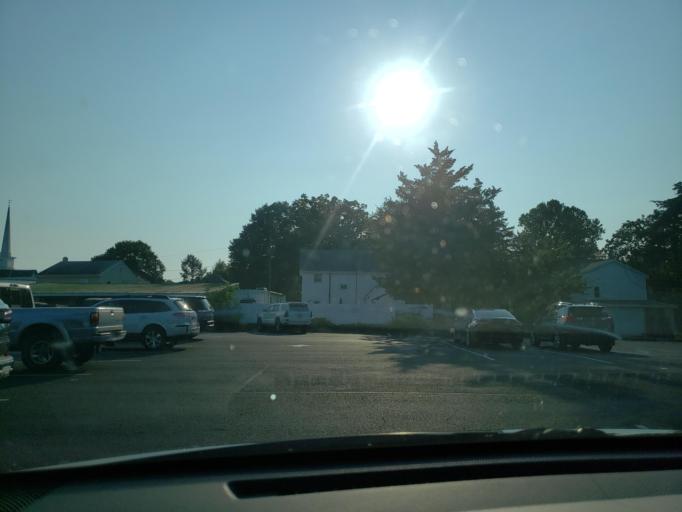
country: US
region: Delaware
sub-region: Kent County
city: Riverview
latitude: 39.0098
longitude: -75.4651
